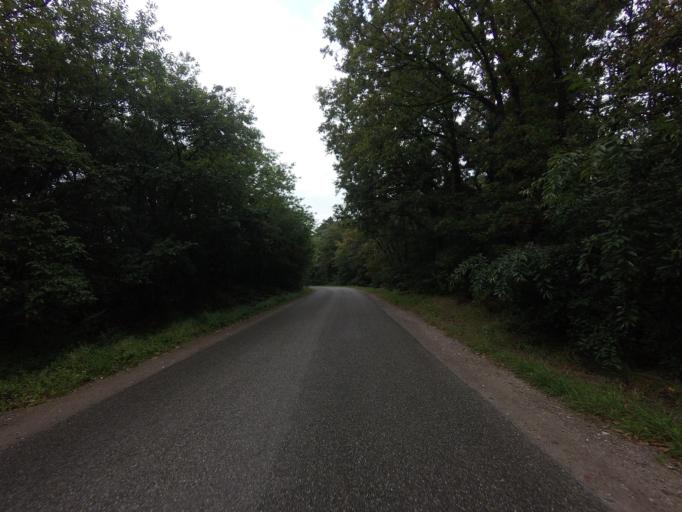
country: NL
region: Overijssel
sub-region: Gemeente Losser
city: Losser
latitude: 52.2618
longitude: 7.0220
